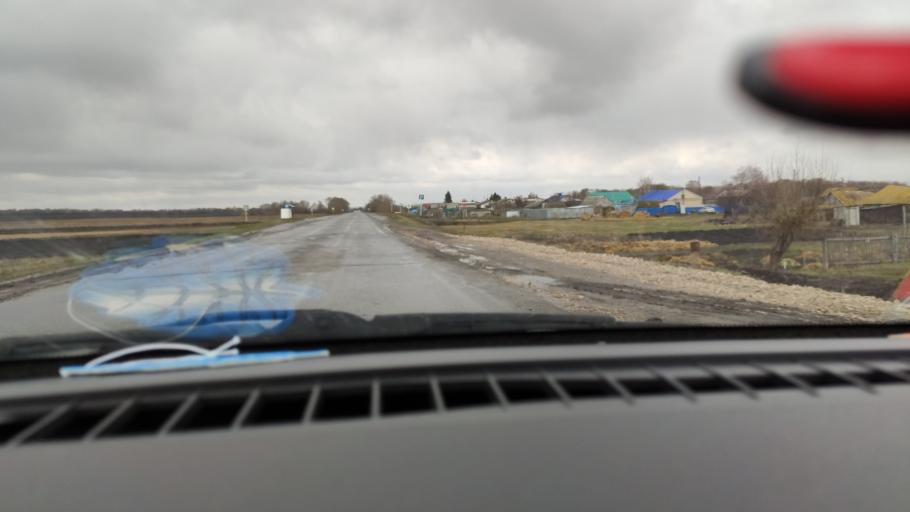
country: RU
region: Samara
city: Koshki
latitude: 54.1653
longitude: 50.4818
